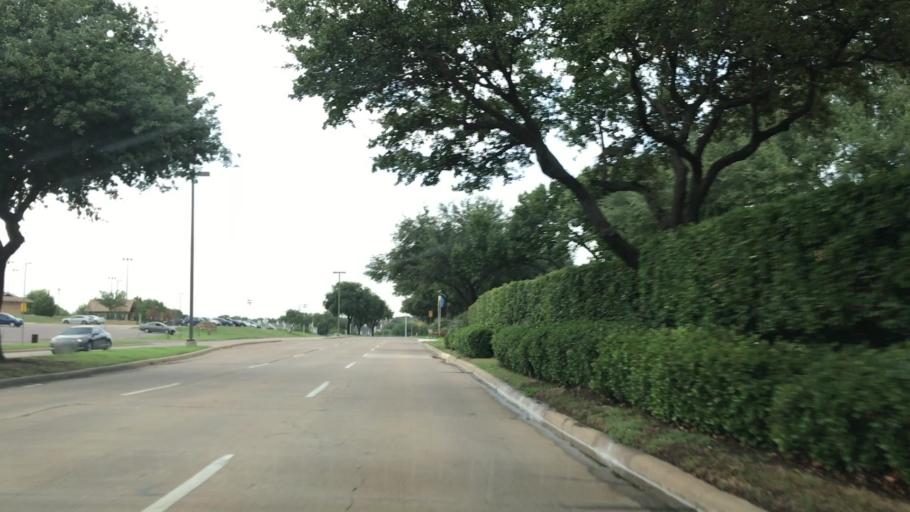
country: US
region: Texas
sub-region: Dallas County
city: Irving
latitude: 32.8608
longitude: -96.9761
